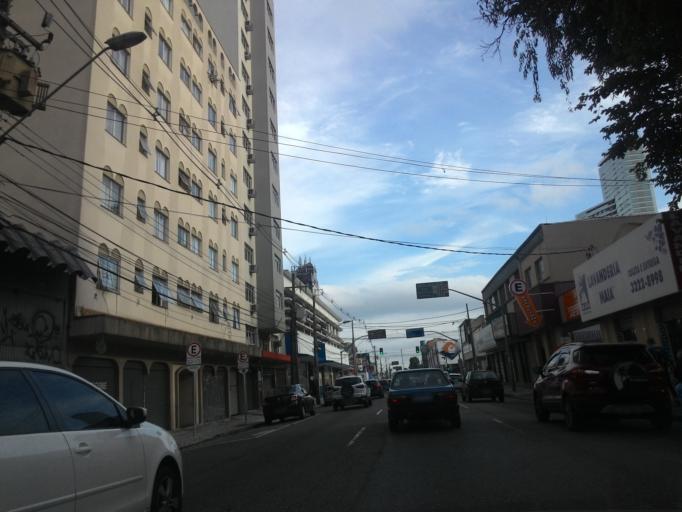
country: BR
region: Parana
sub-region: Curitiba
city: Curitiba
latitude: -25.4333
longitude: -49.2623
